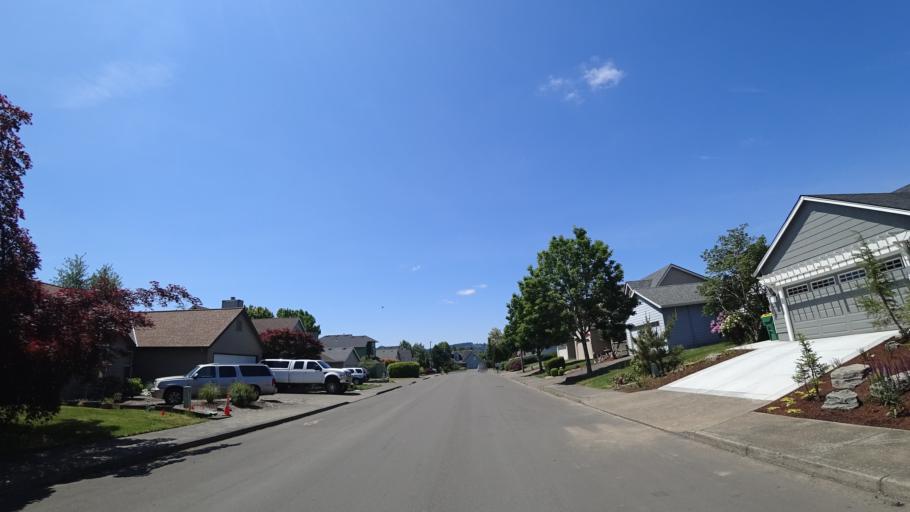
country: US
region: Oregon
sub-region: Washington County
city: Tigard
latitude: 45.4401
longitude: -122.8032
